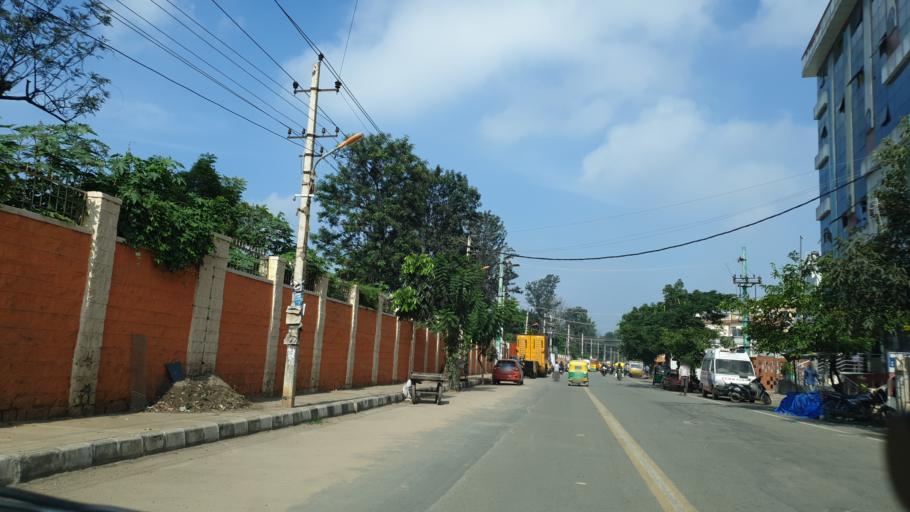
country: IN
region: Karnataka
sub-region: Bangalore Urban
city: Bangalore
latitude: 12.9733
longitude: 77.6755
